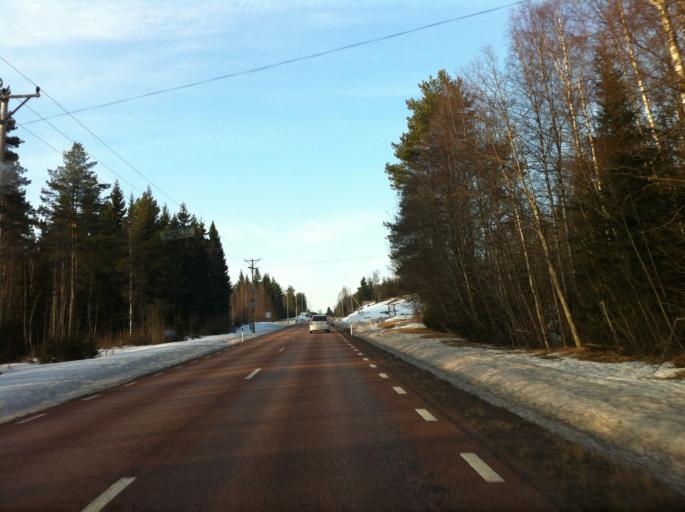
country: SE
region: Dalarna
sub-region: Vansbro Kommun
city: Vansbro
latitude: 60.2603
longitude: 14.1726
